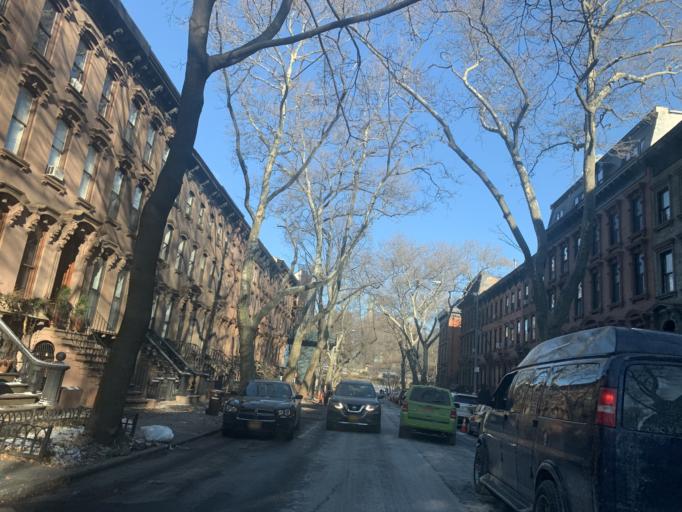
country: US
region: New York
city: New York City
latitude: 40.6886
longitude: -73.9749
